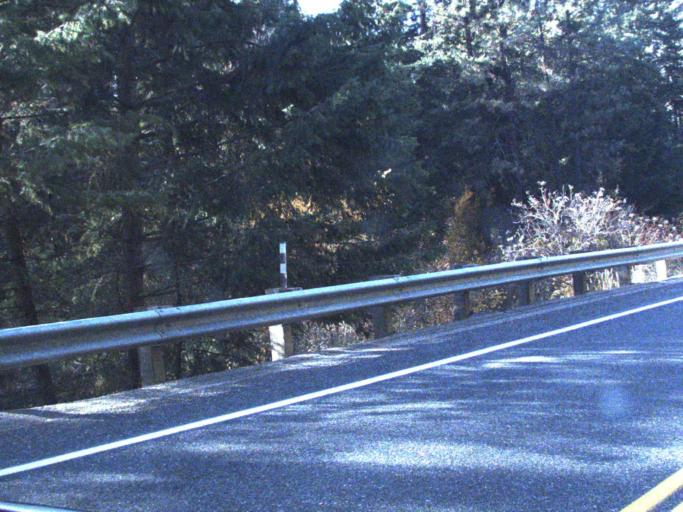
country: US
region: Washington
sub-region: Stevens County
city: Kettle Falls
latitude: 48.4812
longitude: -118.1728
